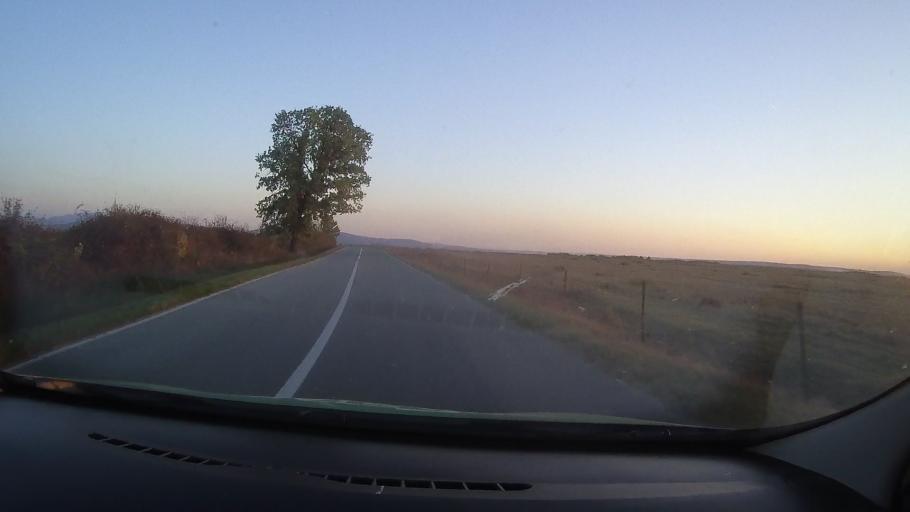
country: RO
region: Timis
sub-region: Comuna Manastiur
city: Manastiur
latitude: 45.8202
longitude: 22.0704
